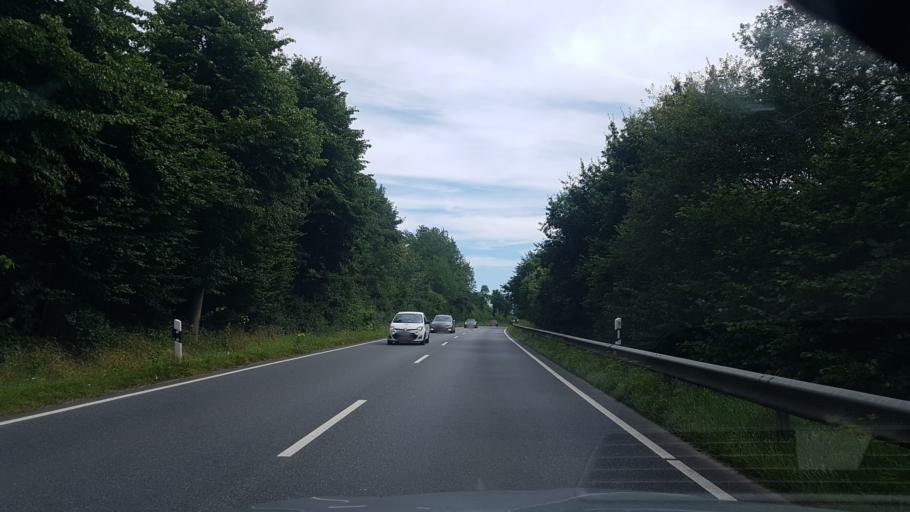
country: DE
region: Schleswig-Holstein
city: Schmalstede
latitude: 54.1884
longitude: 10.0335
